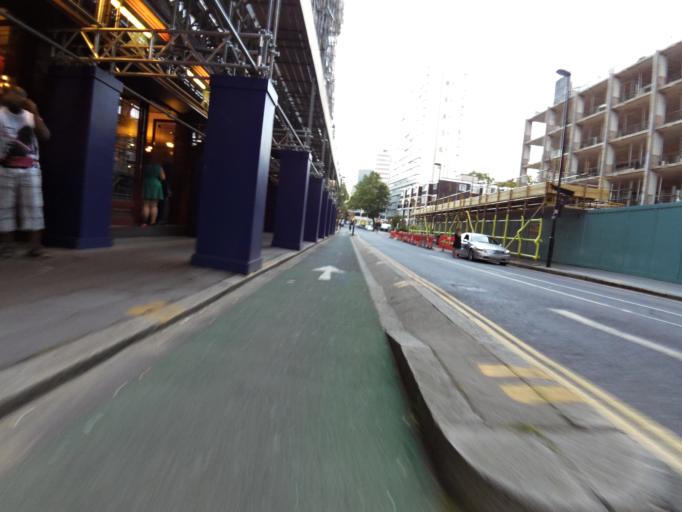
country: GB
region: England
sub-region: Greater London
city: Barbican
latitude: 51.5251
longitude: -0.0907
